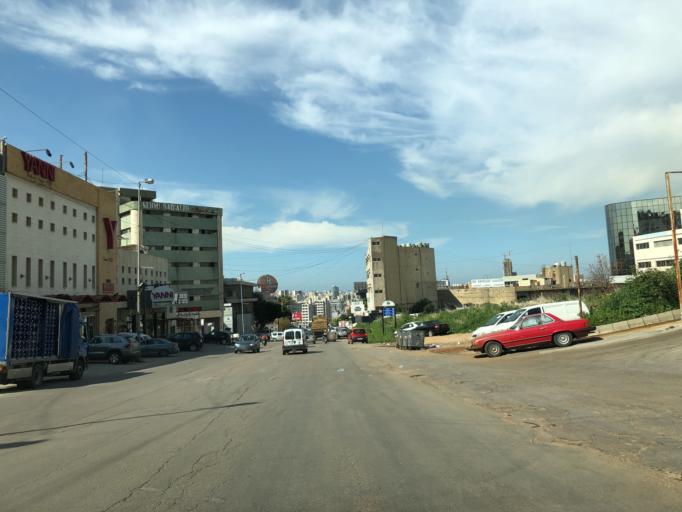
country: LB
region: Mont-Liban
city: Baabda
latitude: 33.8643
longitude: 35.5468
